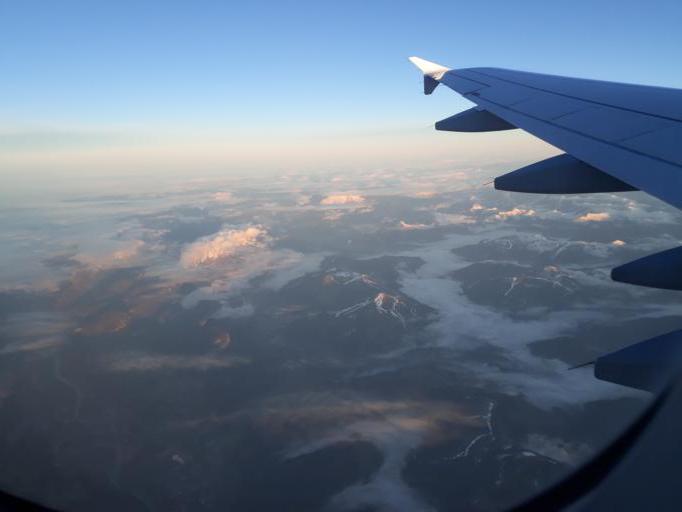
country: AT
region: Tyrol
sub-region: Politischer Bezirk Kufstein
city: Radfeld
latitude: 47.4351
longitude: 11.9386
